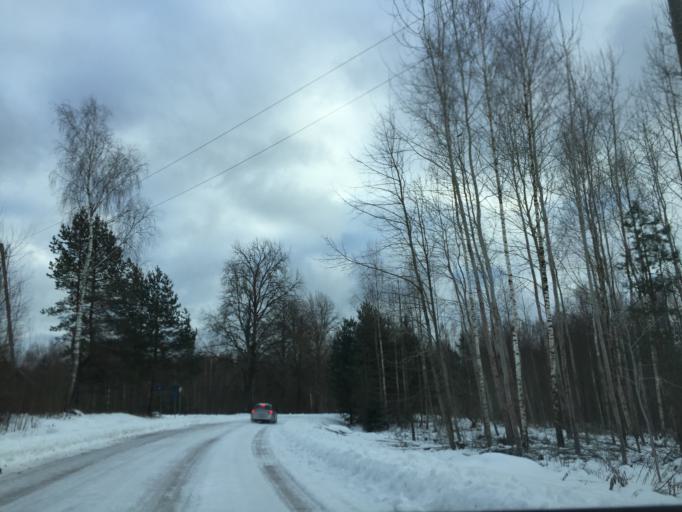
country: LV
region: Lielvarde
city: Lielvarde
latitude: 56.5801
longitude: 24.7860
